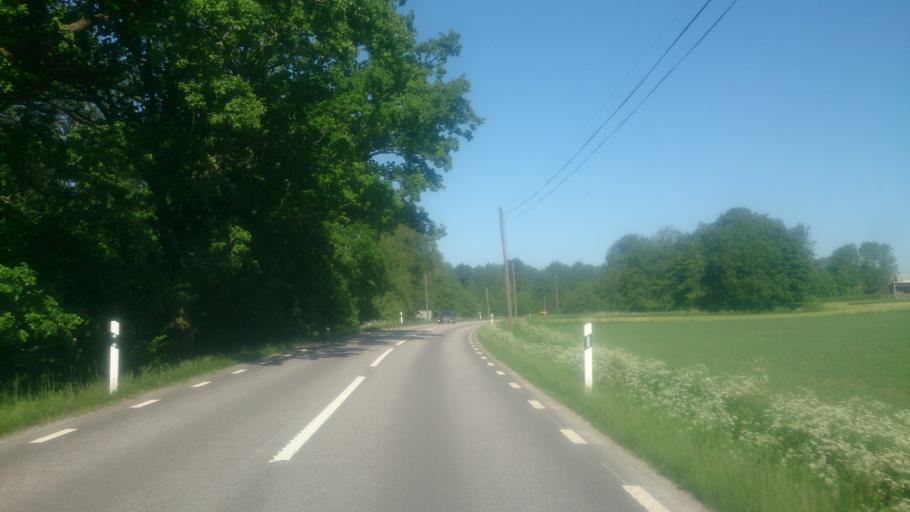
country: SE
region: OEstergoetland
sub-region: Atvidabergs Kommun
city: Atvidaberg
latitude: 58.1403
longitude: 16.0847
